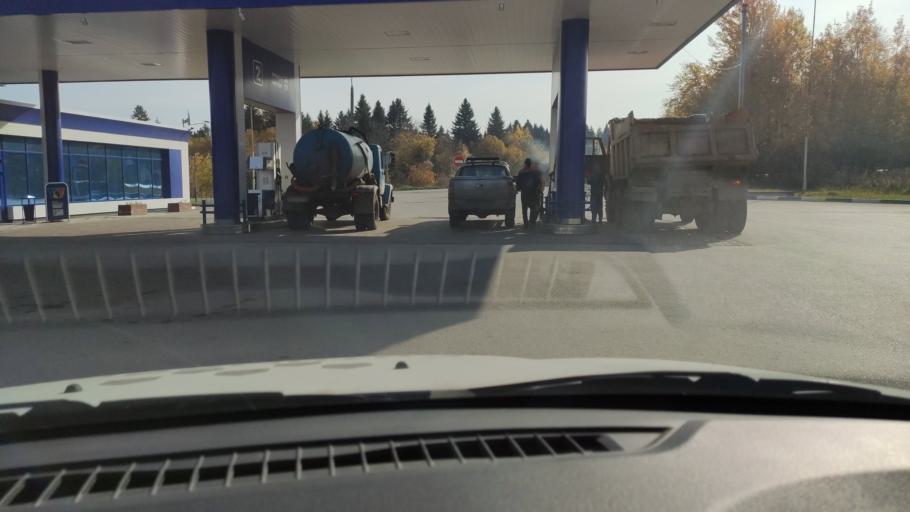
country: RU
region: Perm
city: Sylva
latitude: 58.0257
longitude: 56.7376
